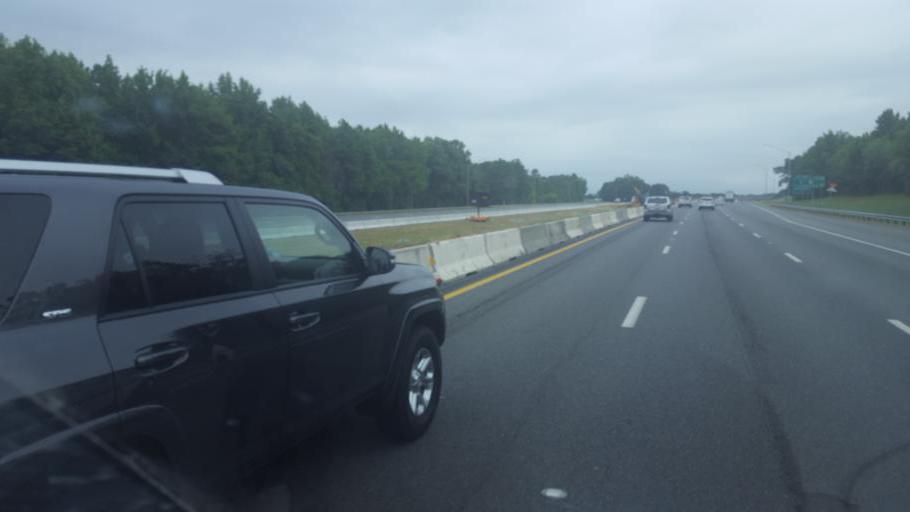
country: US
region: North Carolina
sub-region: Mecklenburg County
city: Huntersville
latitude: 35.3414
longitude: -80.8485
